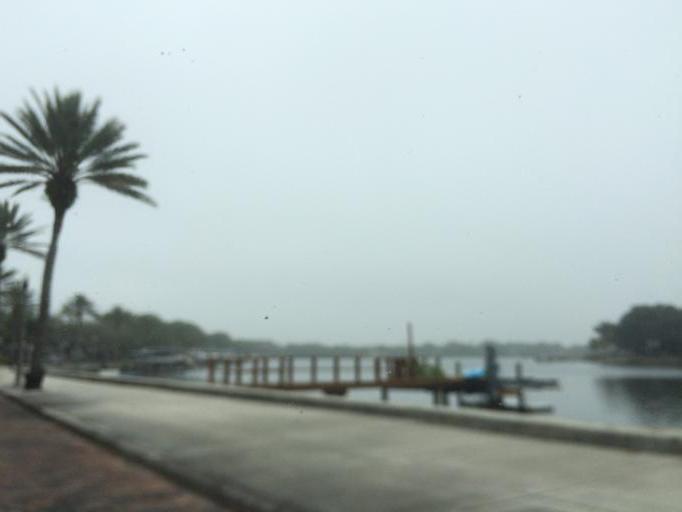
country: US
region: Florida
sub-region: Pinellas County
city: Saint Petersburg
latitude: 27.7950
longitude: -82.6324
